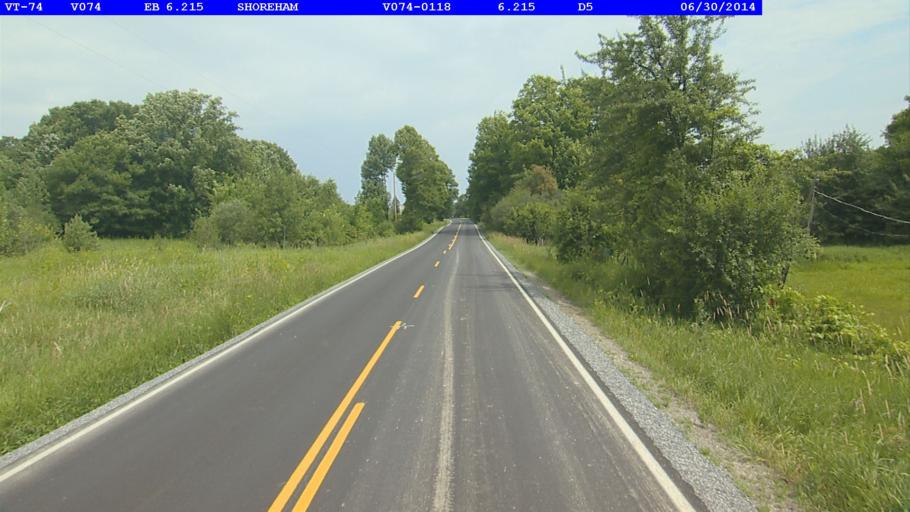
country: US
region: New York
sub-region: Essex County
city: Ticonderoga
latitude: 43.9094
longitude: -73.2968
